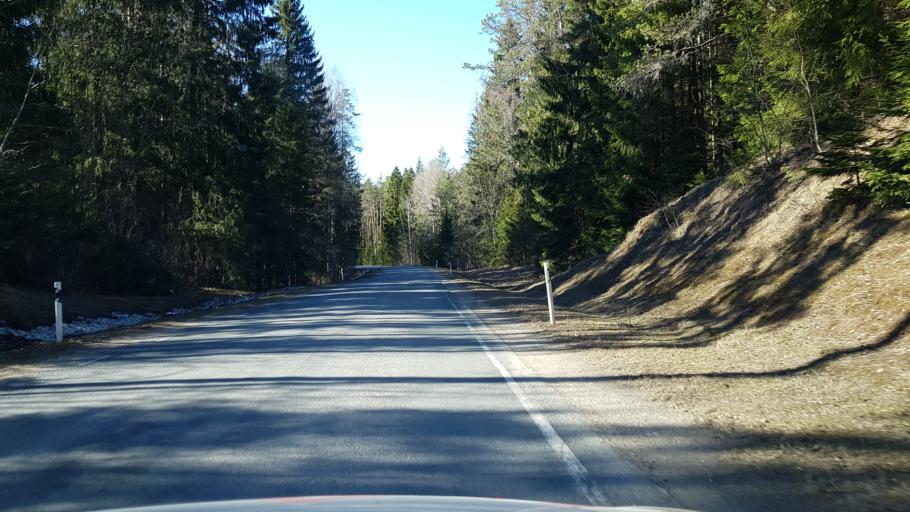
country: EE
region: Laeaene-Virumaa
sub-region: Vinni vald
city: Vinni
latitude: 59.2705
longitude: 26.6633
